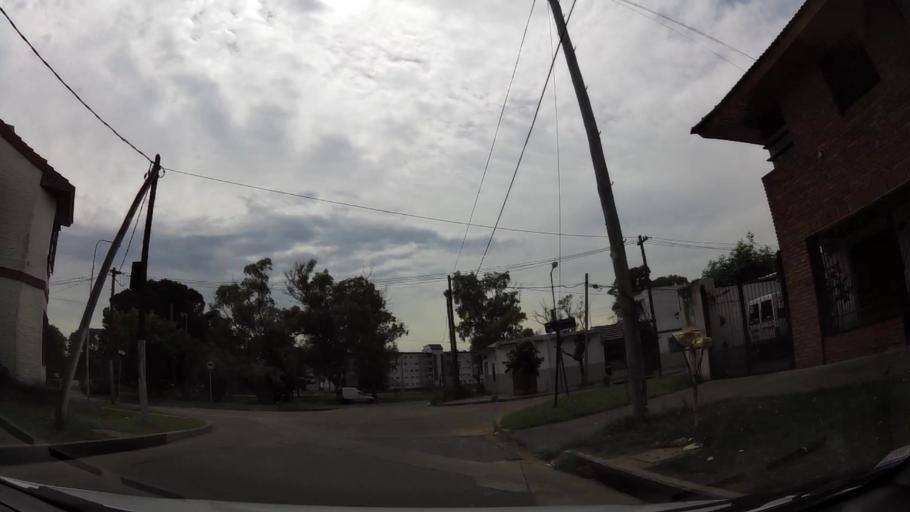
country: AR
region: Buenos Aires F.D.
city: Villa Lugano
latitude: -34.6828
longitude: -58.4923
